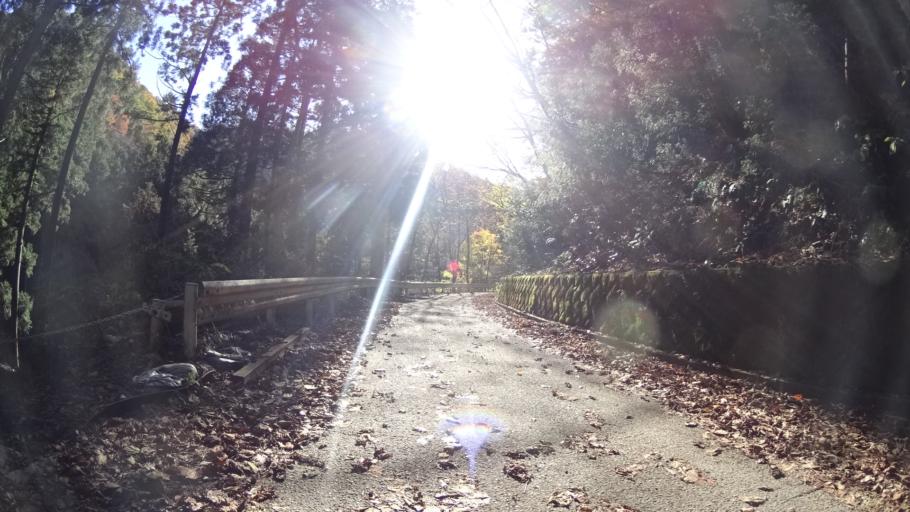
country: JP
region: Kanagawa
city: Atsugi
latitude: 35.5162
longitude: 139.2733
